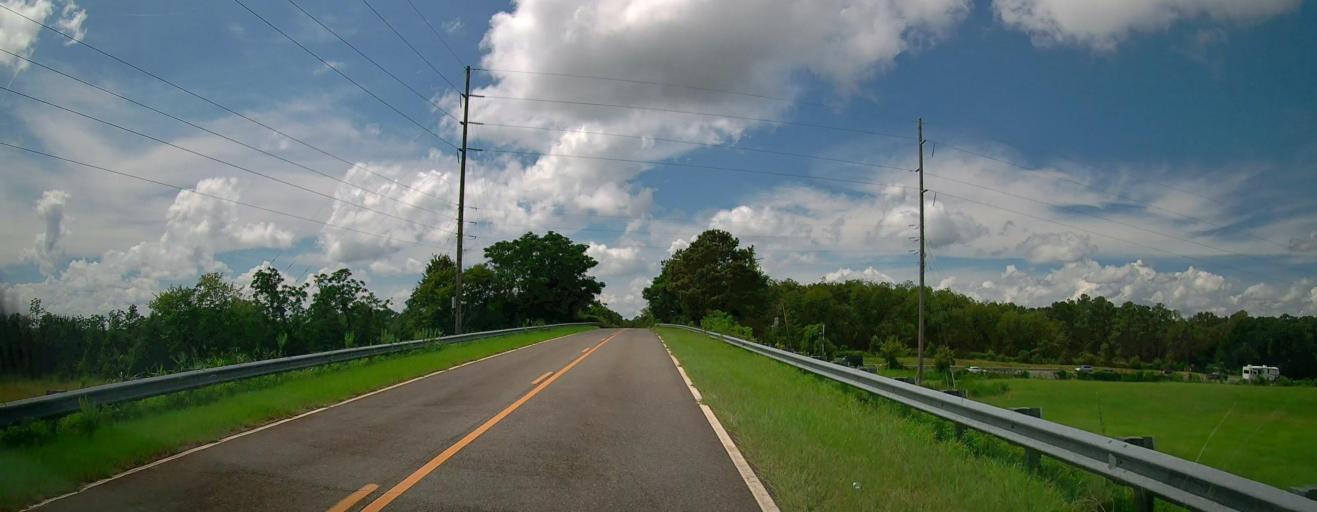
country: US
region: Georgia
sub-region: Houston County
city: Perry
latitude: 32.5110
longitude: -83.7412
